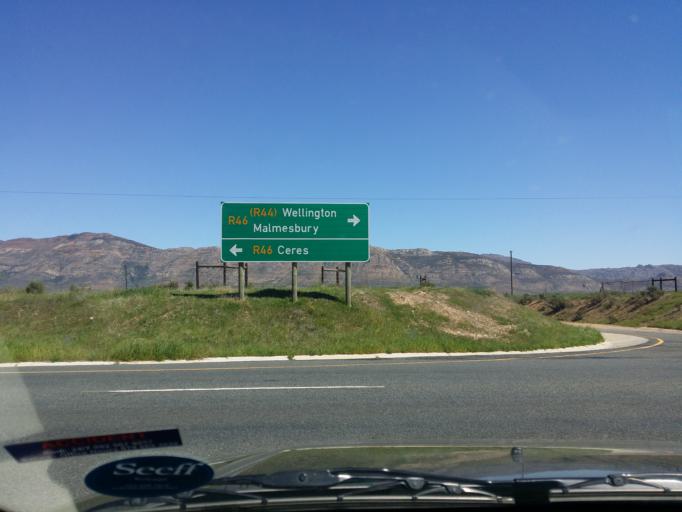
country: ZA
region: Western Cape
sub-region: Cape Winelands District Municipality
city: Ceres
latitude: -33.3636
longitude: 19.1704
